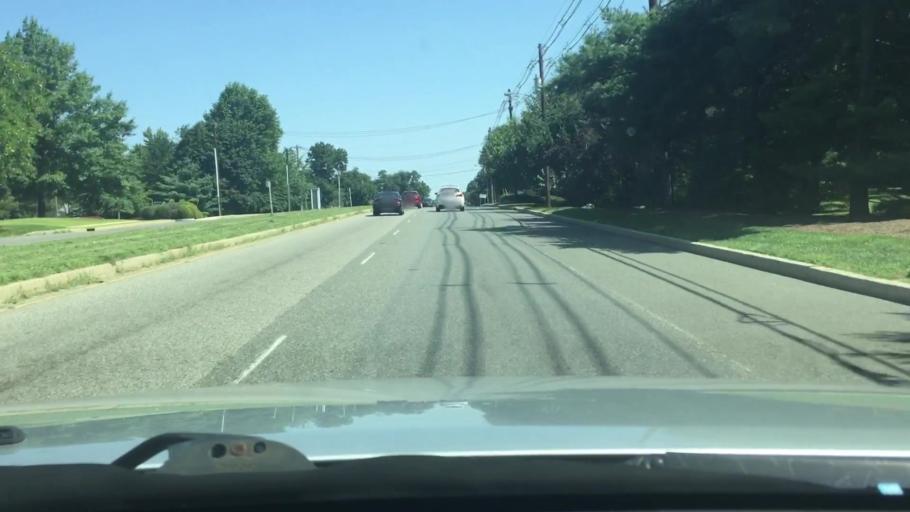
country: US
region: New Jersey
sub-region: Middlesex County
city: East Brunswick
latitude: 40.4107
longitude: -74.4190
